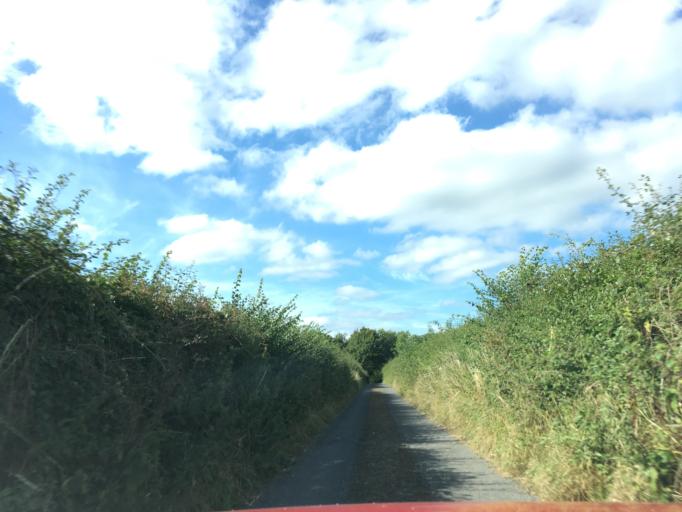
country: IE
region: Munster
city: Cashel
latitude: 52.4606
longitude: -7.9416
